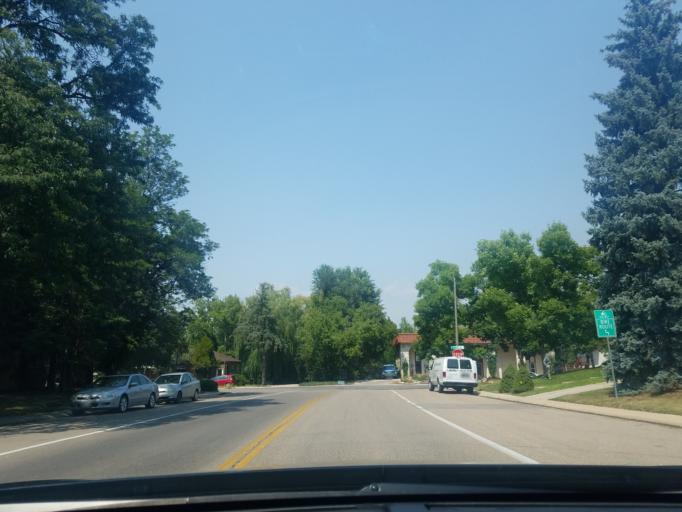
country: US
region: Colorado
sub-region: Larimer County
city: Fort Collins
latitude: 40.5630
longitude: -105.0668
